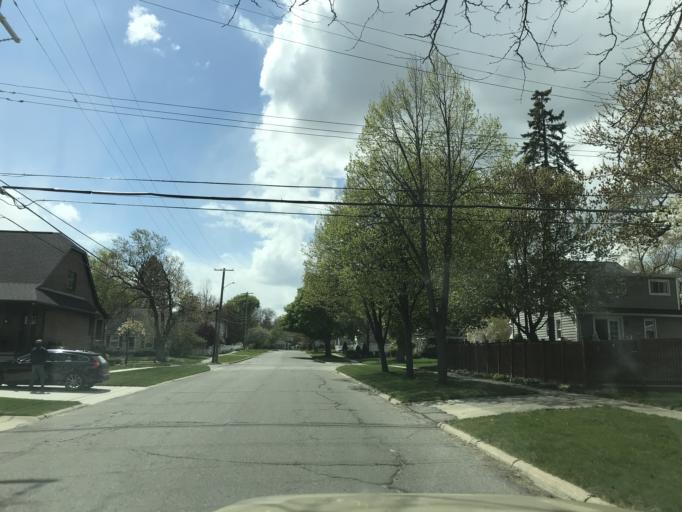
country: US
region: Michigan
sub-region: Wayne County
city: Plymouth
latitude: 42.3777
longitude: -83.4772
